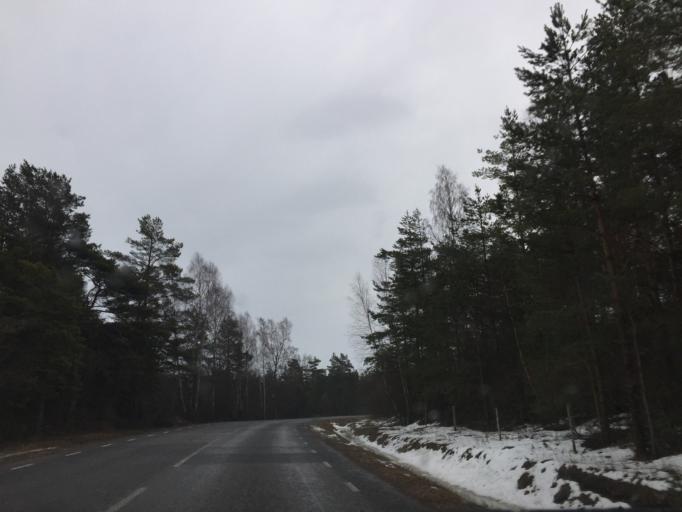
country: EE
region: Saare
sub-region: Orissaare vald
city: Orissaare
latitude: 58.6069
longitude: 22.9655
